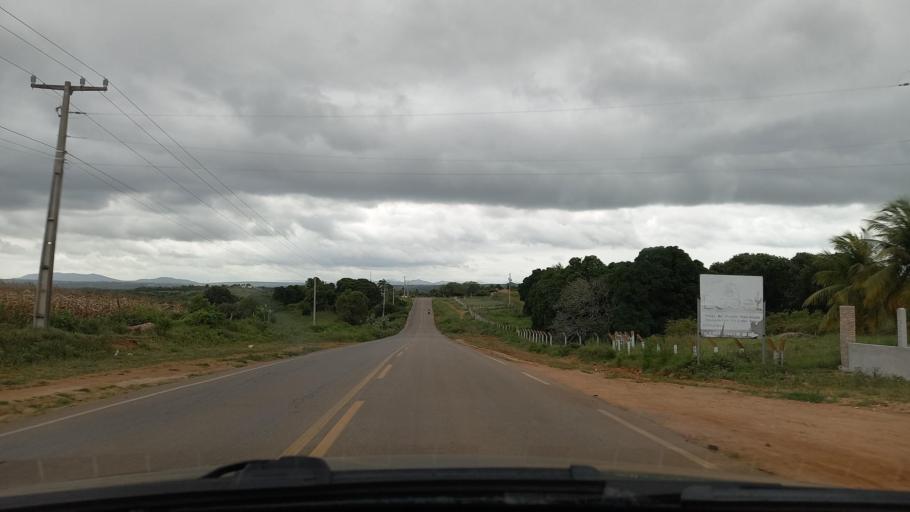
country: BR
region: Sergipe
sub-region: Caninde De Sao Francisco
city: Caninde de Sao Francisco
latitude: -9.6819
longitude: -37.8099
